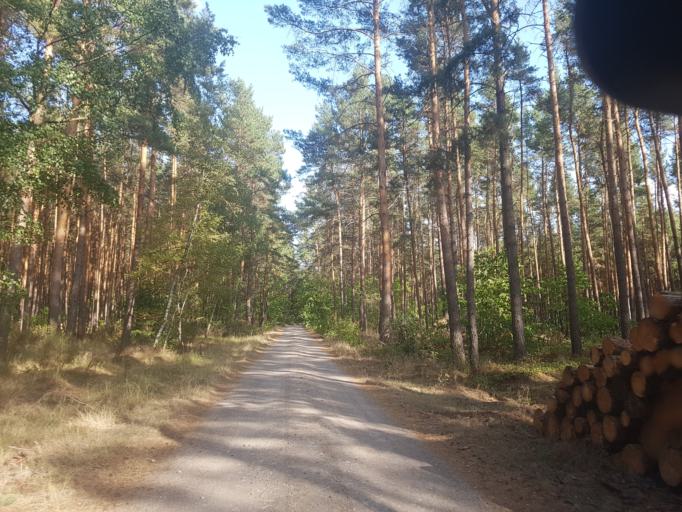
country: DE
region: Saxony-Anhalt
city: Jessen
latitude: 51.8667
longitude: 13.0246
